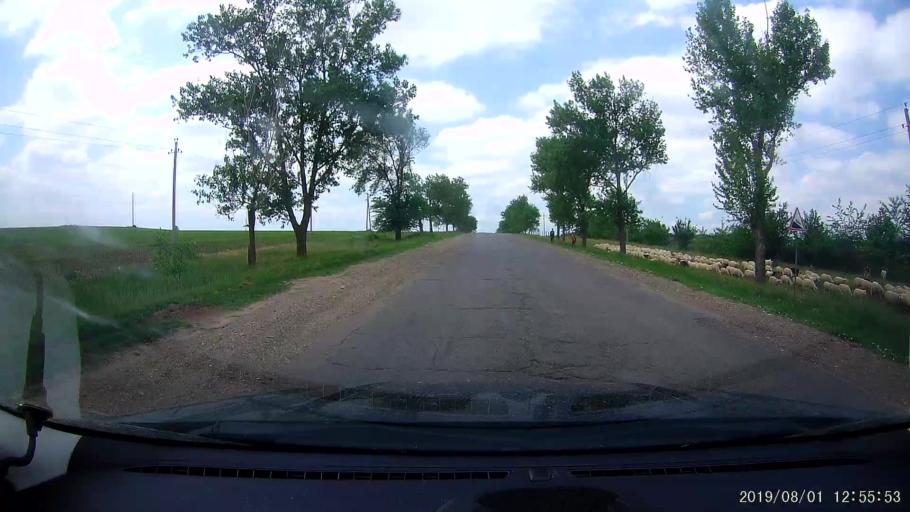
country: MD
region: Gagauzia
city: Vulcanesti
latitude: 45.6930
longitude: 28.4579
